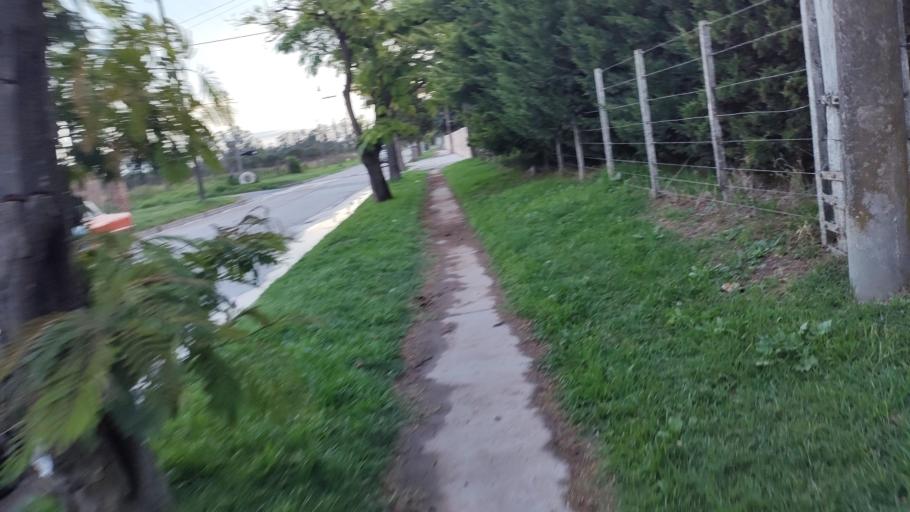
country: AR
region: Buenos Aires
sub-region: Partido de Loberia
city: Loberia
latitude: -38.1764
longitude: -58.7769
